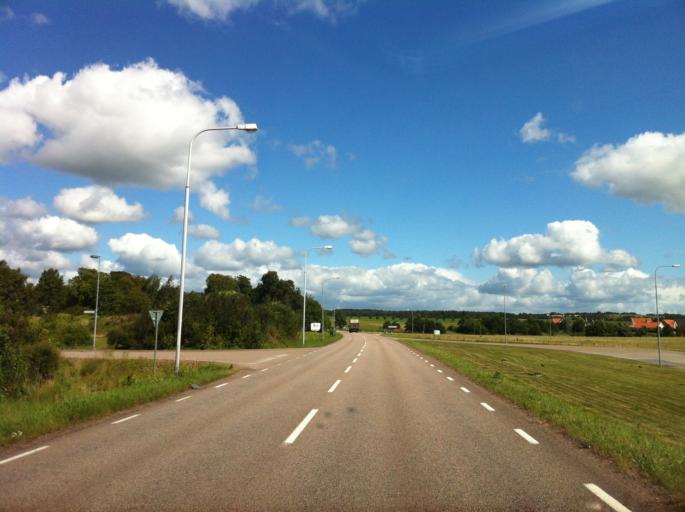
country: SE
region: Skane
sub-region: Svalovs Kommun
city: Svaloev
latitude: 55.9185
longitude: 13.1034
